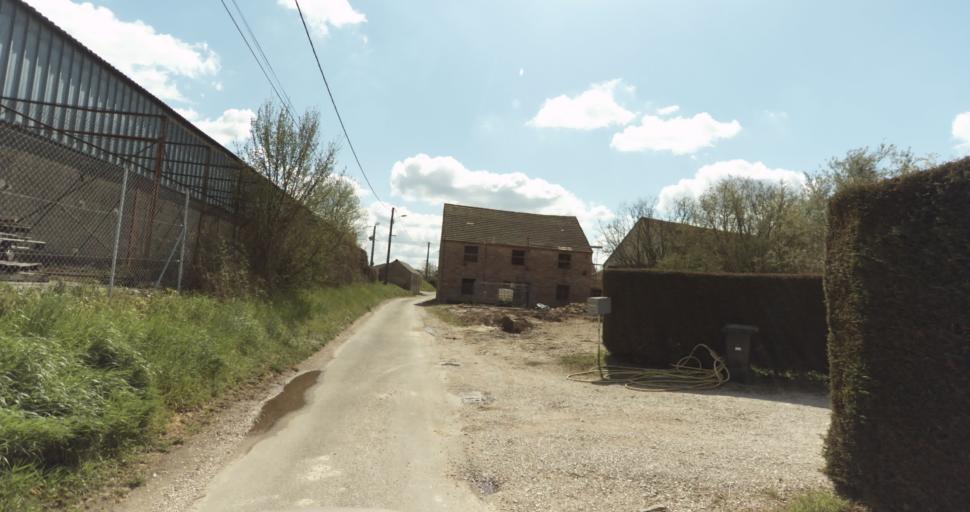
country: FR
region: Bourgogne
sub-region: Departement de la Cote-d'Or
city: Auxonne
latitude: 47.2104
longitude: 5.4121
